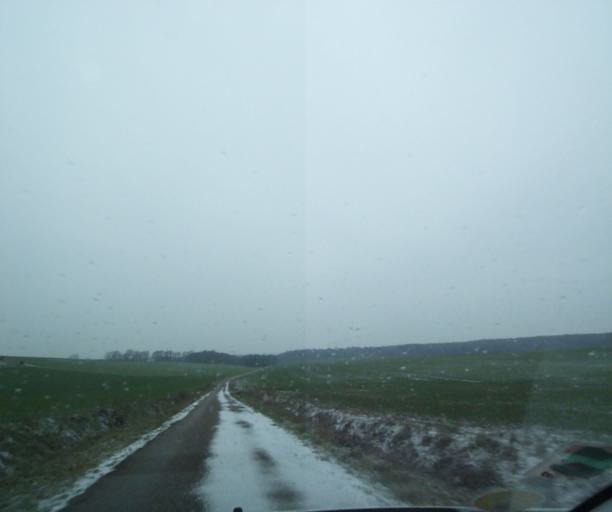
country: FR
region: Champagne-Ardenne
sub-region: Departement de la Haute-Marne
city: Wassy
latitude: 48.4624
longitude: 5.0260
